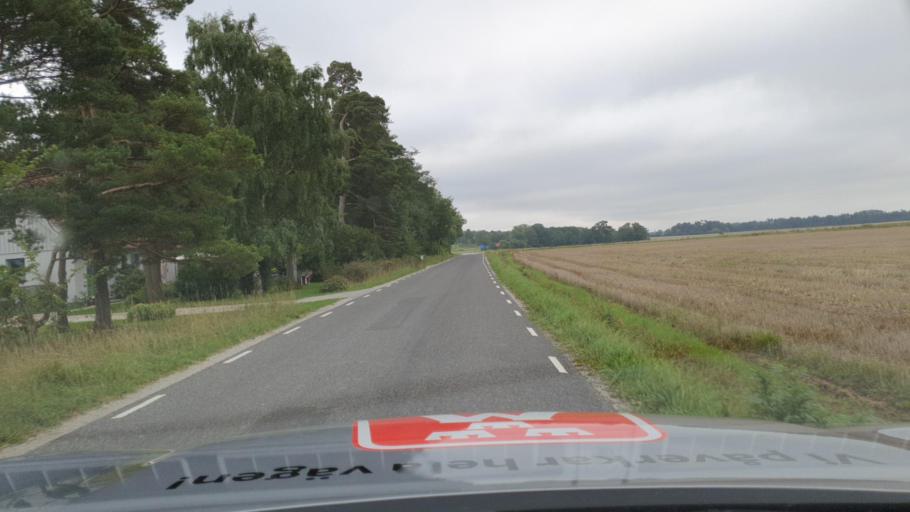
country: SE
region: Gotland
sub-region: Gotland
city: Visby
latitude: 57.6148
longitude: 18.4649
